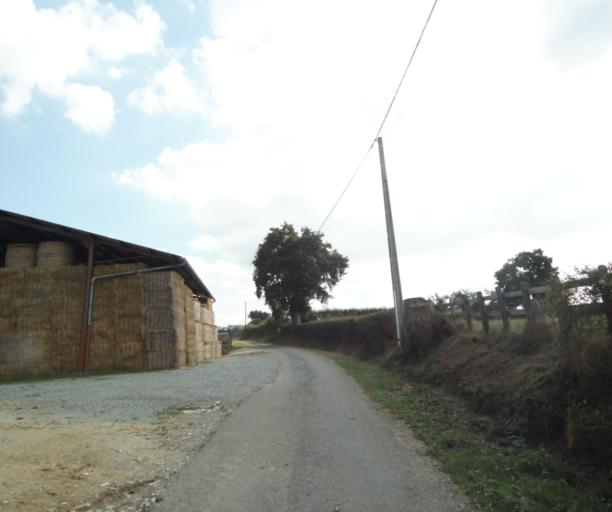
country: FR
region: Bourgogne
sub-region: Departement de Saone-et-Loire
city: Charolles
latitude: 46.3565
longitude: 4.2427
